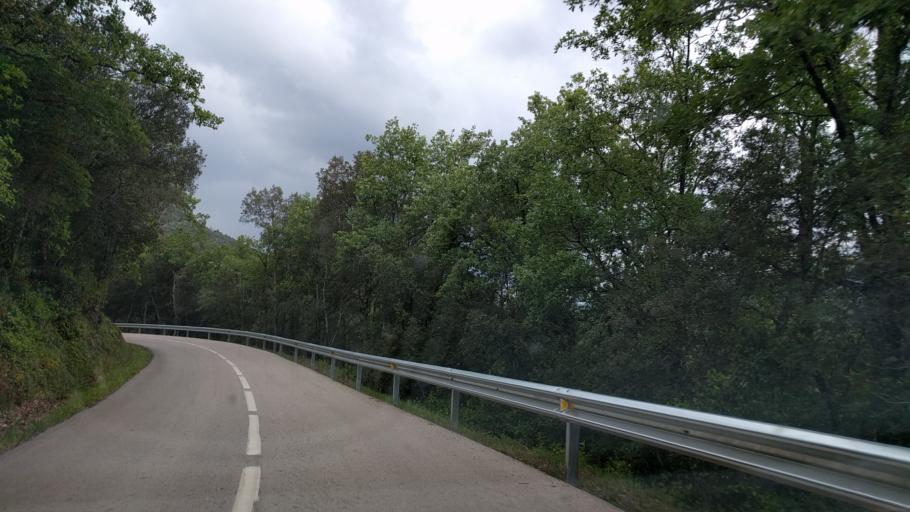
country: ES
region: Catalonia
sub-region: Provincia de Girona
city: la Cellera de Ter
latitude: 42.0149
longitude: 2.6734
